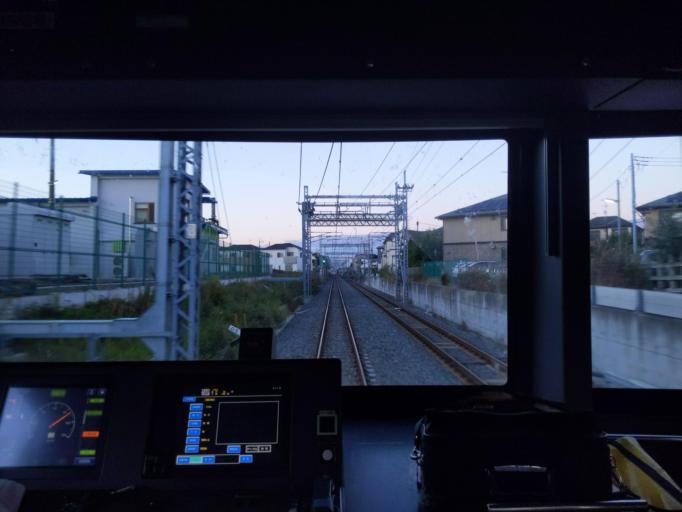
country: JP
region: Chiba
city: Kashiwa
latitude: 35.7978
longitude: 139.9992
